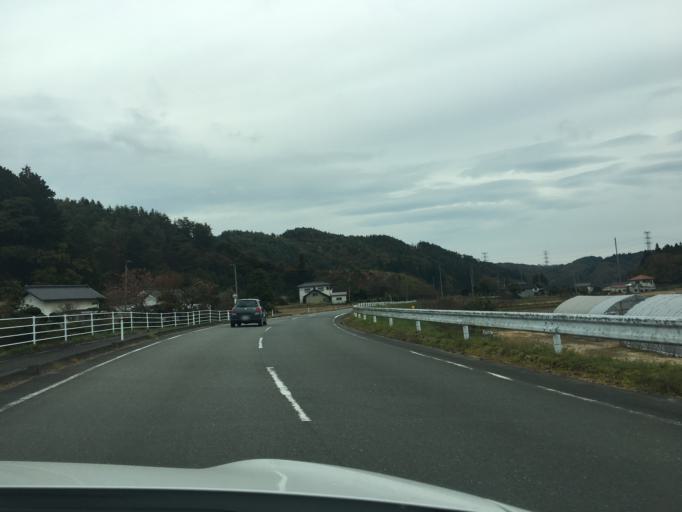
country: JP
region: Fukushima
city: Iwaki
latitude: 37.1575
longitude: 140.7447
